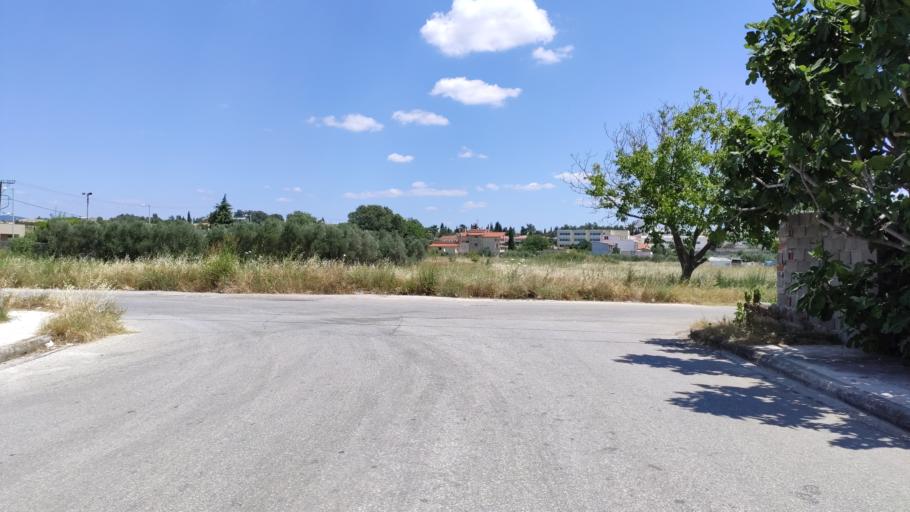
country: GR
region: East Macedonia and Thrace
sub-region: Nomos Rodopis
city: Komotini
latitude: 41.1299
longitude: 25.4025
